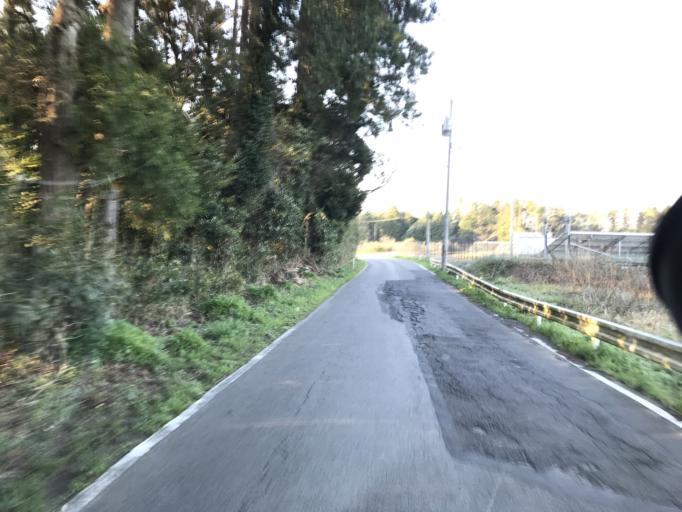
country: JP
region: Chiba
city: Yokaichiba
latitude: 35.7803
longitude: 140.5347
